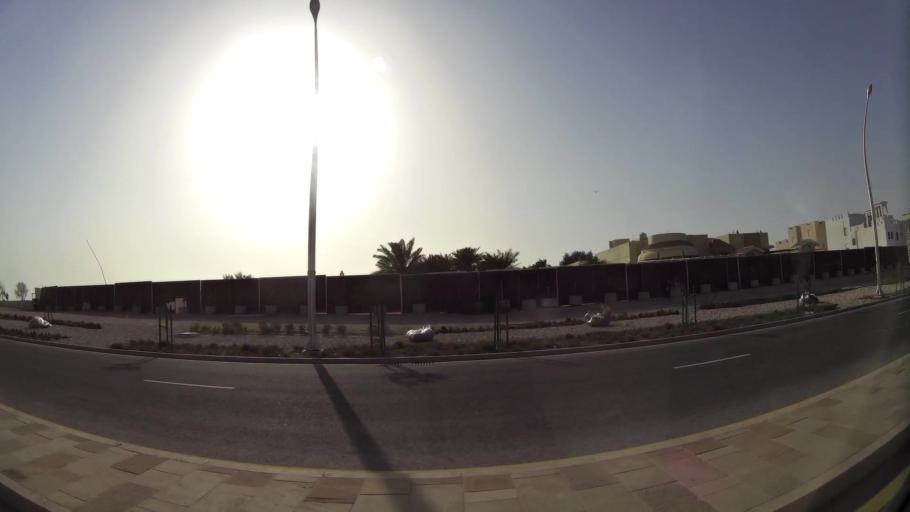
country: QA
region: Baladiyat ar Rayyan
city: Ar Rayyan
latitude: 25.3288
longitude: 51.4306
